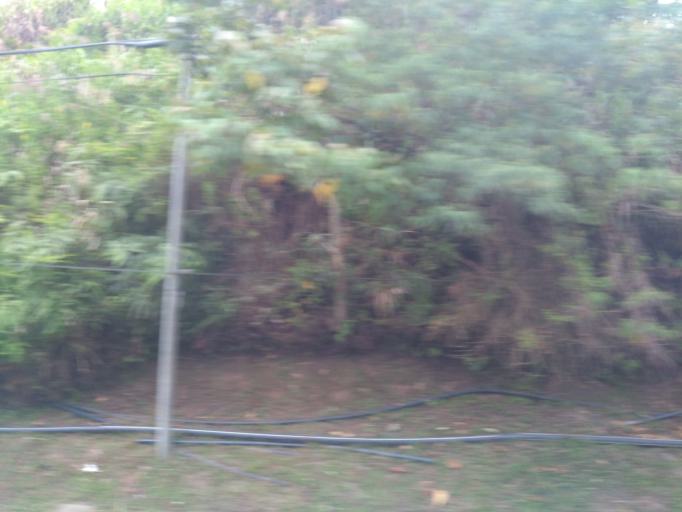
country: MY
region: Pahang
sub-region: Cameron Highlands
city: Tanah Rata
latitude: 4.5787
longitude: 101.4153
